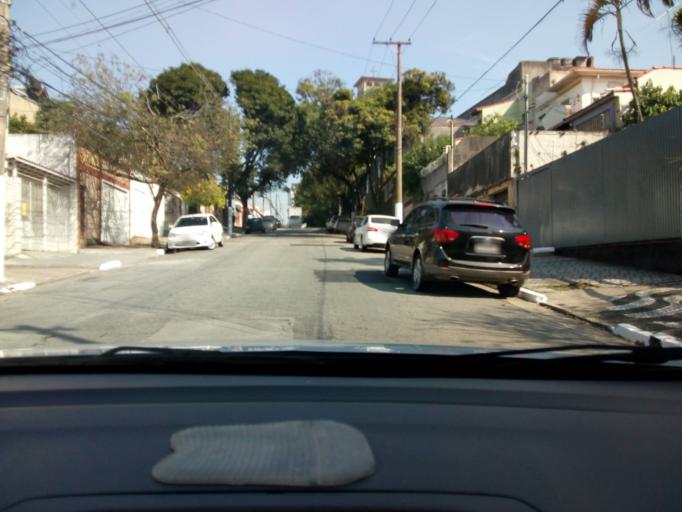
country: BR
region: Sao Paulo
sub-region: Sao Paulo
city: Sao Paulo
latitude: -23.5821
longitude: -46.6248
